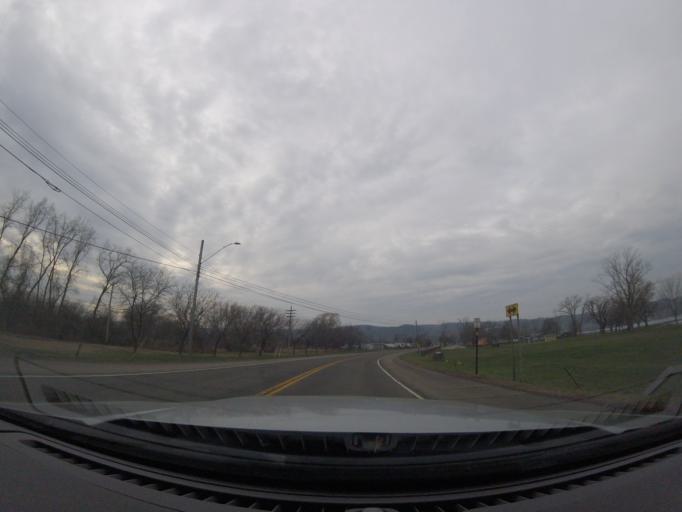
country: US
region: New York
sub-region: Schuyler County
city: Watkins Glen
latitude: 42.3861
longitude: -76.8558
